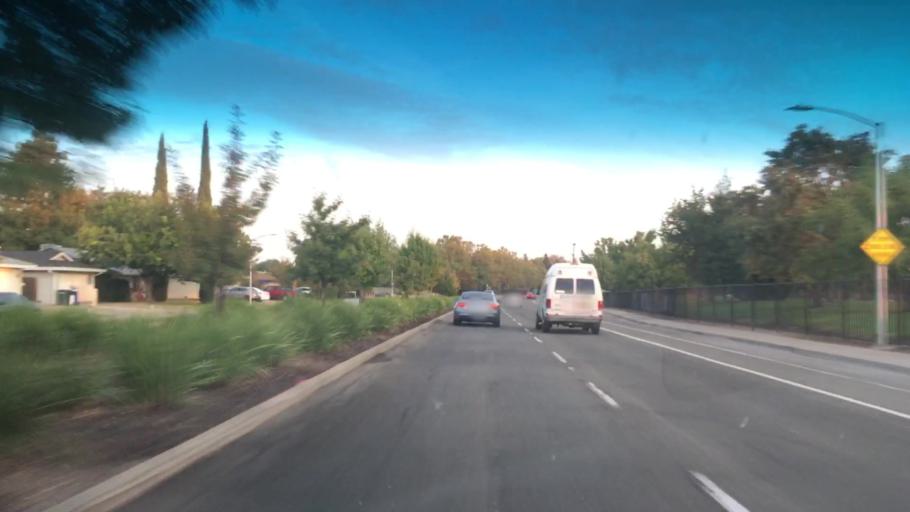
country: US
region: California
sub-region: Sacramento County
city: Laguna
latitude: 38.4511
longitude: -121.4265
